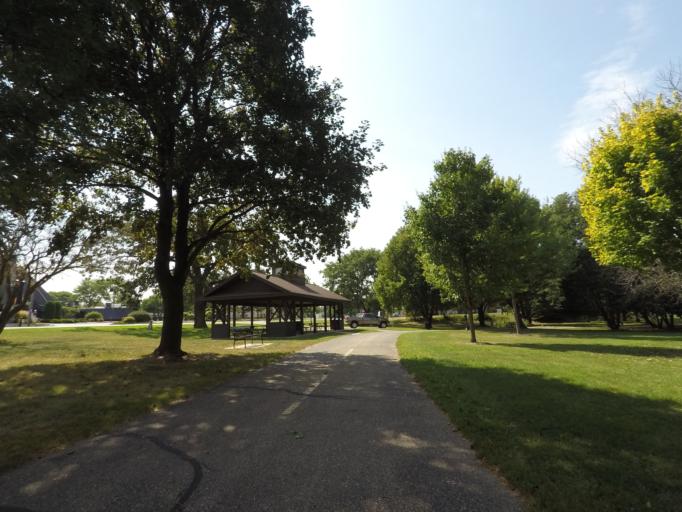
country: US
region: Wisconsin
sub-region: Jefferson County
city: Fort Atkinson
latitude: 42.9148
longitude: -88.8494
